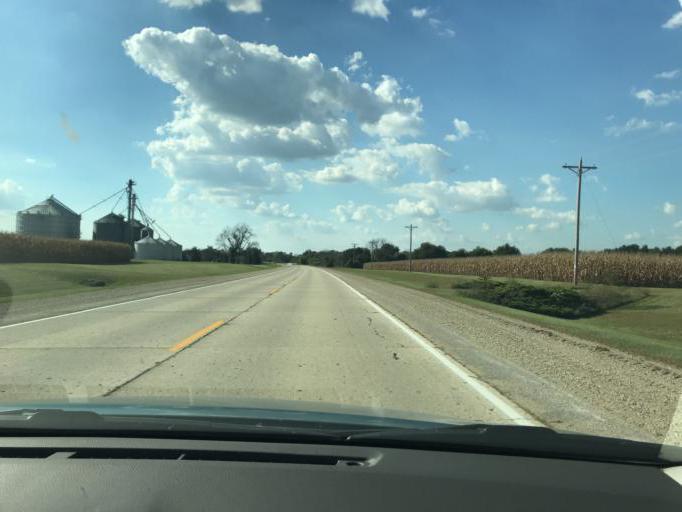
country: US
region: Wisconsin
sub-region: Green County
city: Brodhead
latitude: 42.5693
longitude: -89.3438
